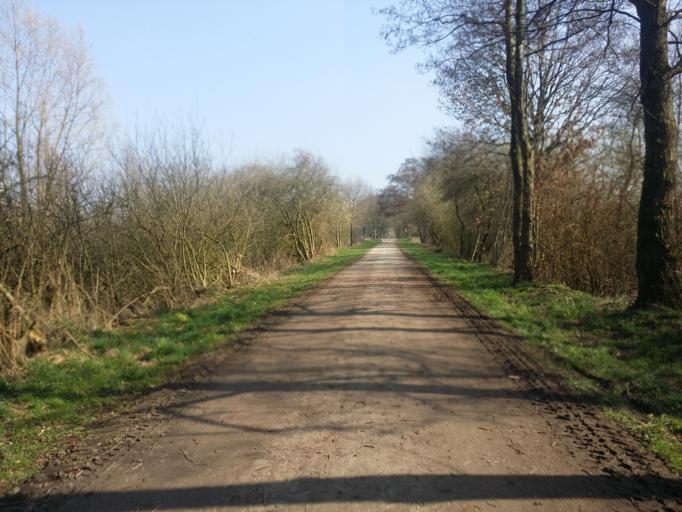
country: DE
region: Lower Saxony
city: Delmenhorst
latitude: 53.0150
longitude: 8.6625
